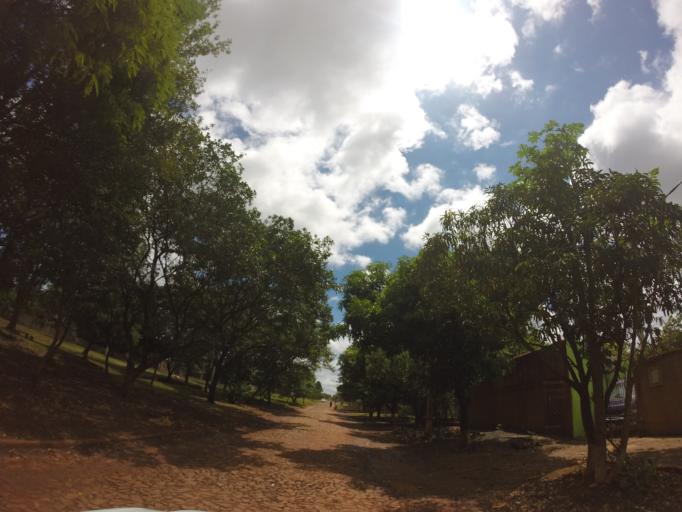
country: PY
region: Alto Parana
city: Ciudad del Este
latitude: -25.3979
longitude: -54.6514
